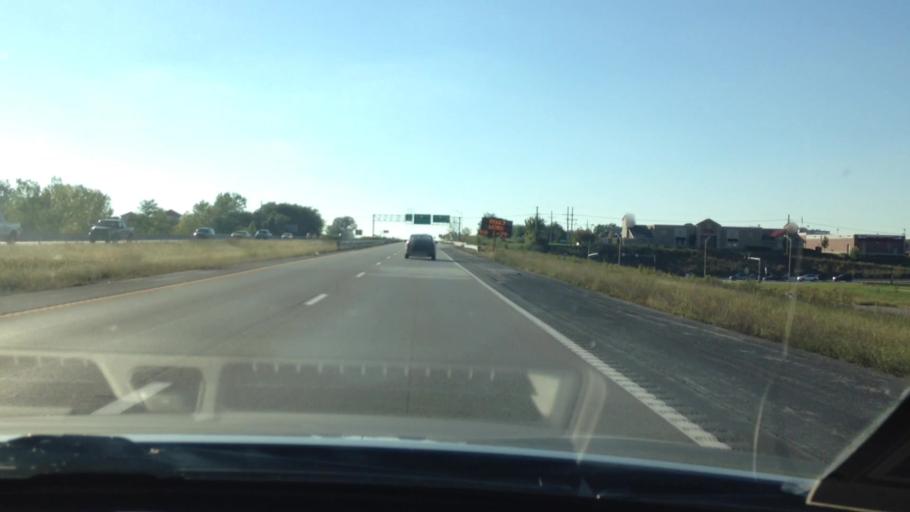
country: US
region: Missouri
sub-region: Platte County
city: Weatherby Lake
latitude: 39.2545
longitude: -94.6469
